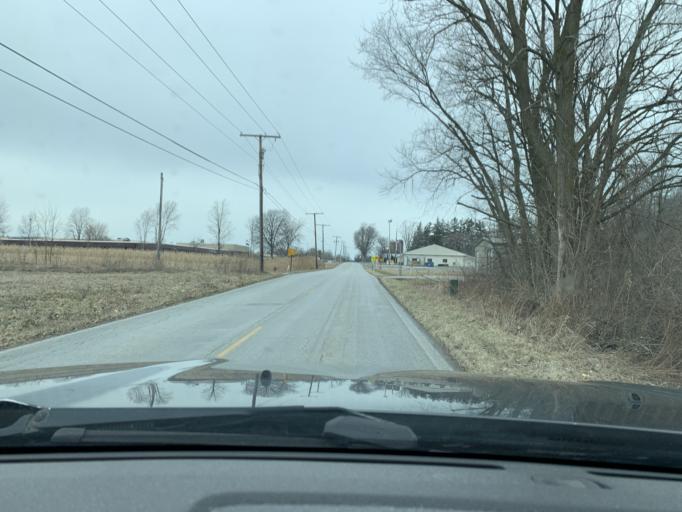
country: US
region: Indiana
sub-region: Porter County
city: Chesterton
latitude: 41.5645
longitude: -87.0731
